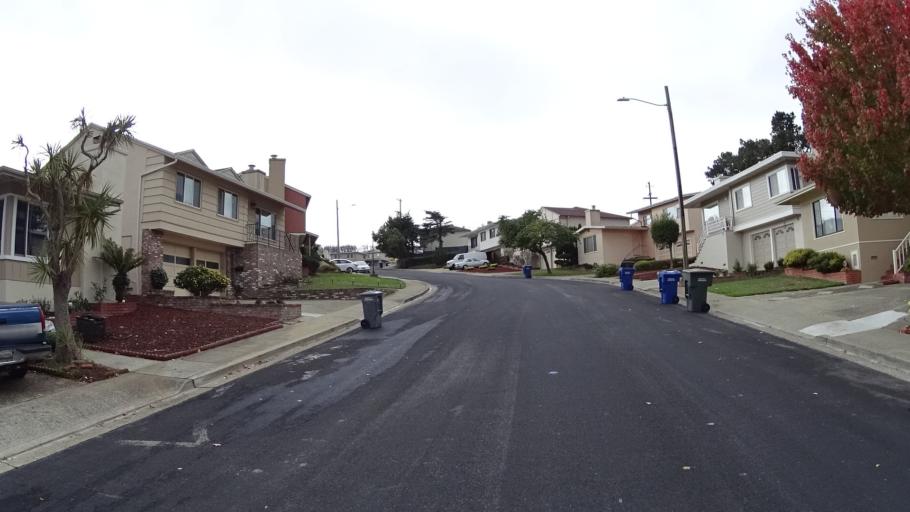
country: US
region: California
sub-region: San Mateo County
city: San Bruno
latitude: 37.6431
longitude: -122.4377
